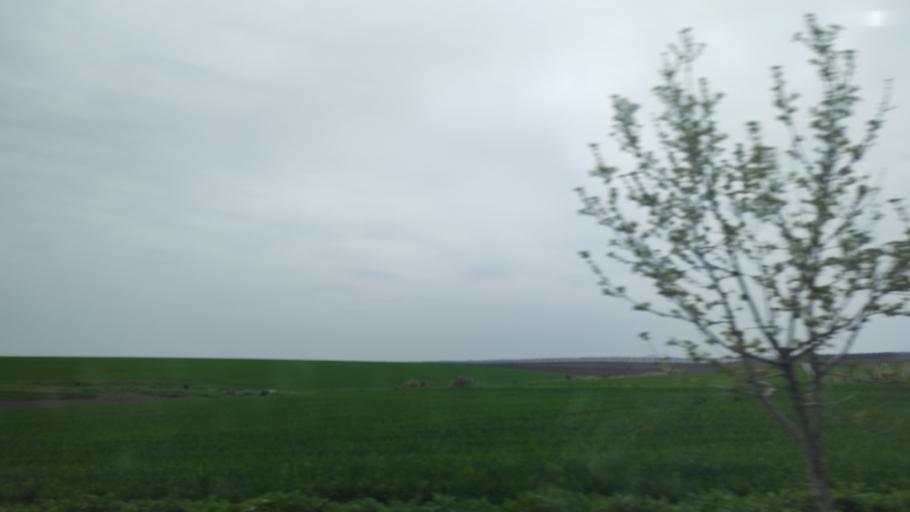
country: RO
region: Constanta
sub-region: Comuna Deleni
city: Pietreni
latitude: 44.0816
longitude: 28.1176
